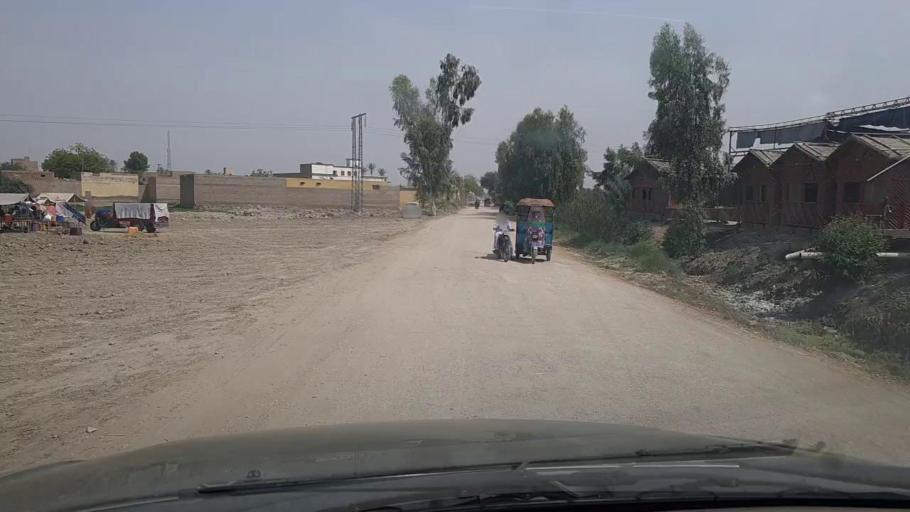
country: PK
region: Sindh
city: Shikarpur
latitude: 27.9307
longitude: 68.6597
